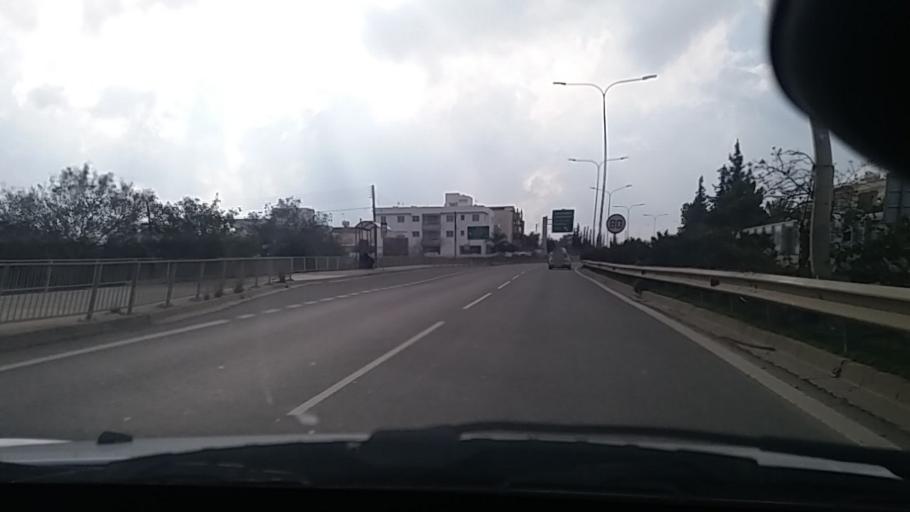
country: CY
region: Lefkosia
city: Kato Deftera
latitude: 35.1316
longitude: 33.3030
